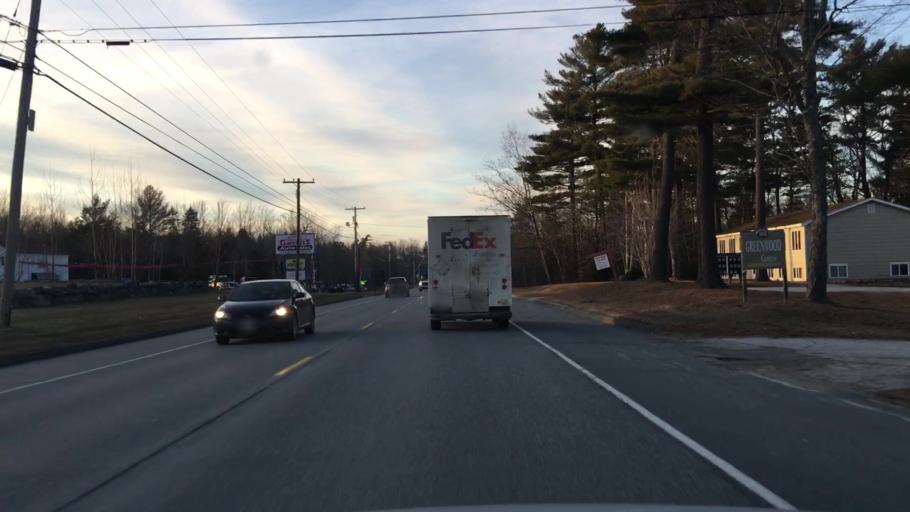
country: US
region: Maine
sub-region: Penobscot County
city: Holden
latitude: 44.7605
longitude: -68.6958
